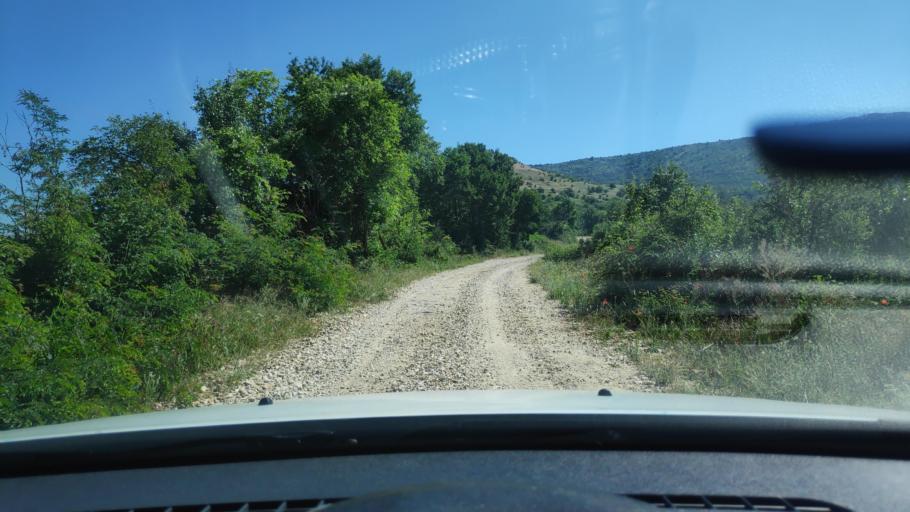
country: MK
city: Klechovce
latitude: 42.0720
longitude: 21.8931
